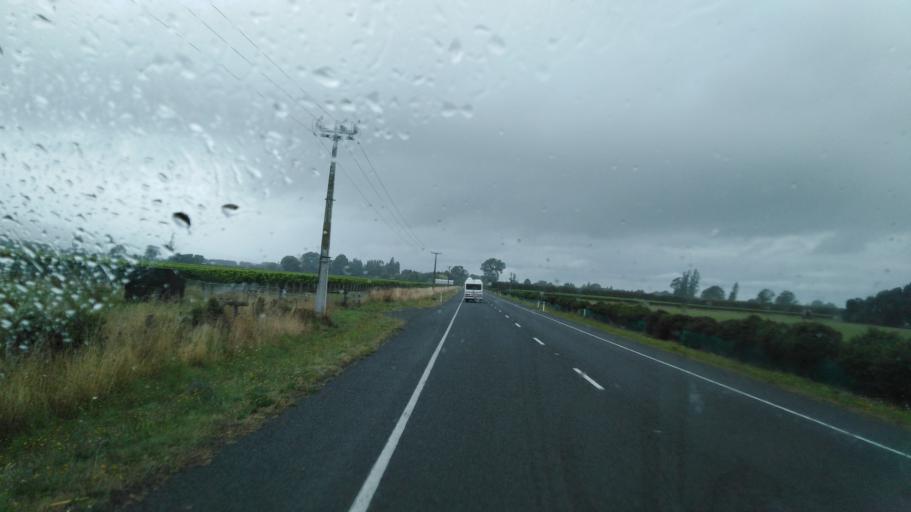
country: NZ
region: Marlborough
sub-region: Marlborough District
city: Blenheim
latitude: -41.4613
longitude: 173.9393
